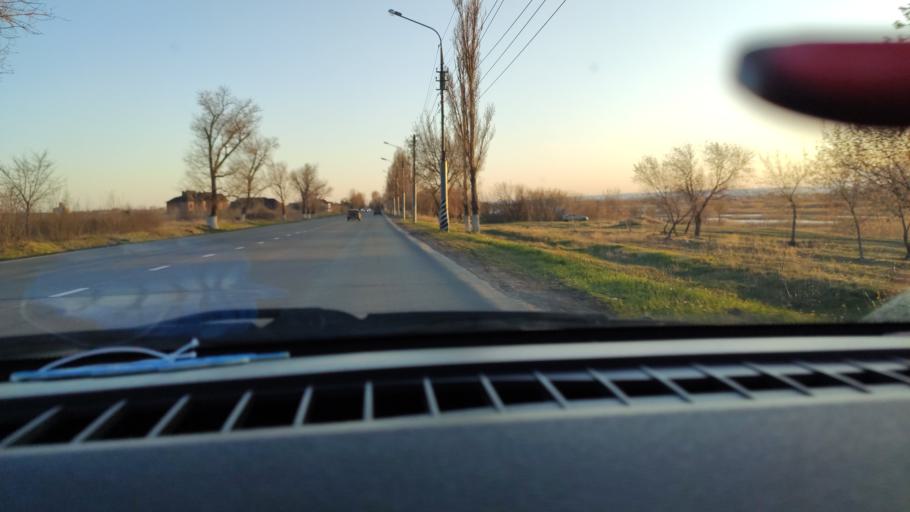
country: RU
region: Saratov
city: Privolzhskiy
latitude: 51.4353
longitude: 46.0602
